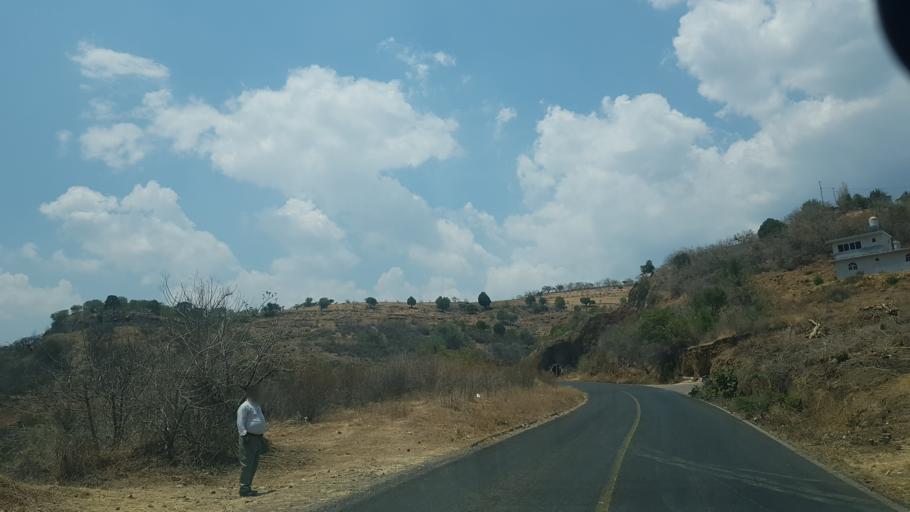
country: MX
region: Puebla
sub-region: Atzitzihuacan
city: Santiago Atzitzihuacan
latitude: 18.8336
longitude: -98.5996
